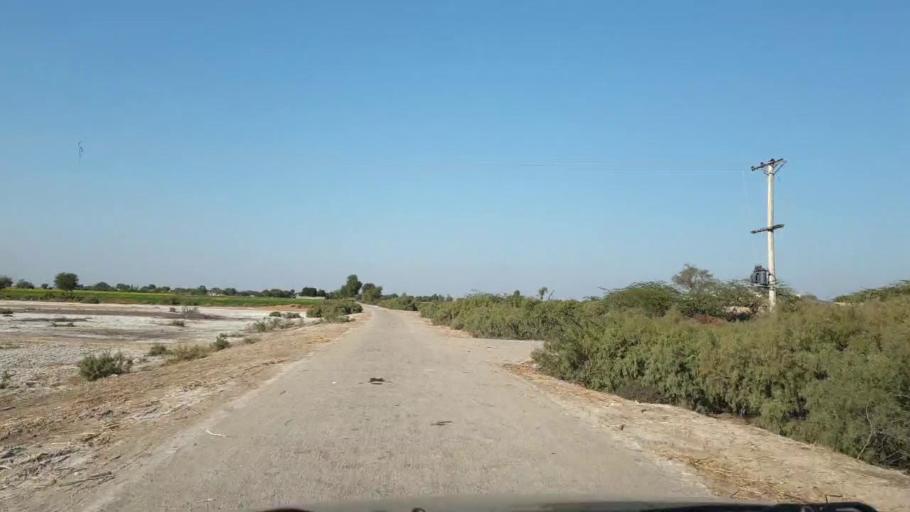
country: PK
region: Sindh
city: Khadro
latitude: 26.2072
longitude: 68.7543
